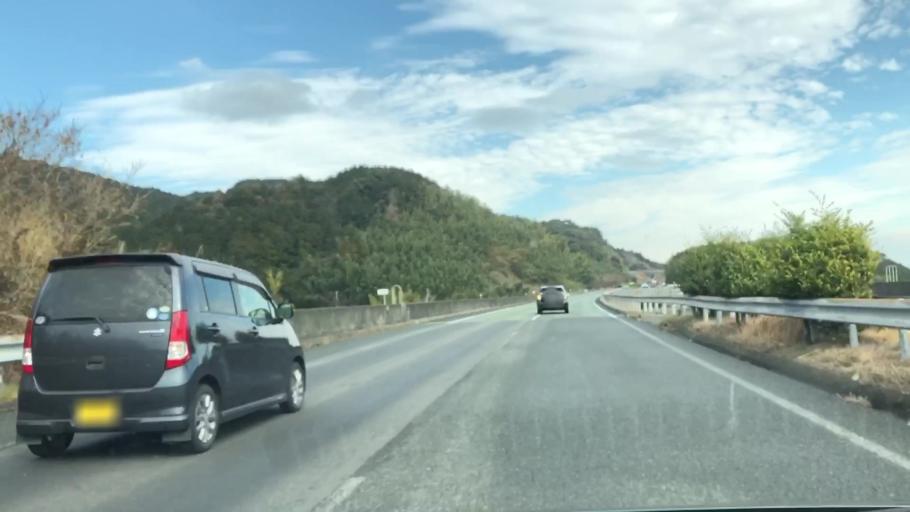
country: JP
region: Saga Prefecture
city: Tosu
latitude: 33.3879
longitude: 130.4852
